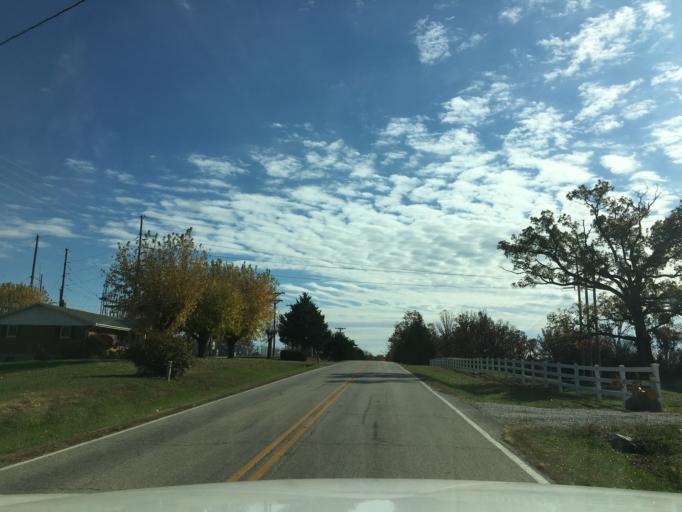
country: US
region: Missouri
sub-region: Osage County
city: Linn
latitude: 38.4291
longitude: -91.8267
